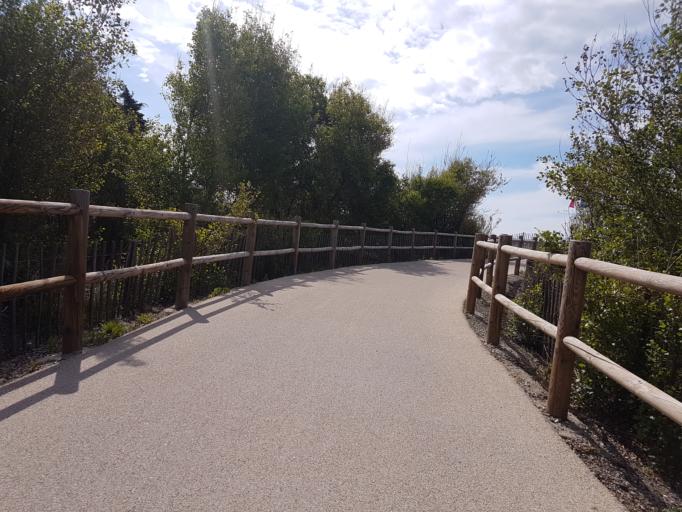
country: FR
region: Languedoc-Roussillon
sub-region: Departement de l'Herault
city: Perols
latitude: 43.5537
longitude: 4.0095
